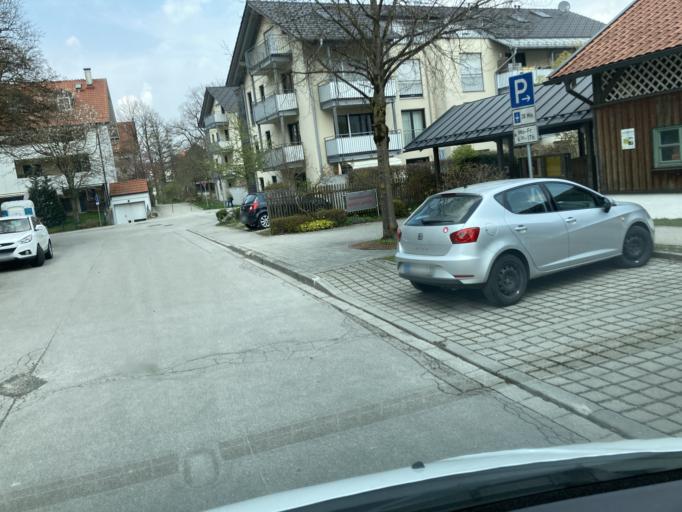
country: DE
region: Bavaria
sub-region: Upper Bavaria
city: Grafing bei Munchen
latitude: 48.0429
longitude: 11.9667
